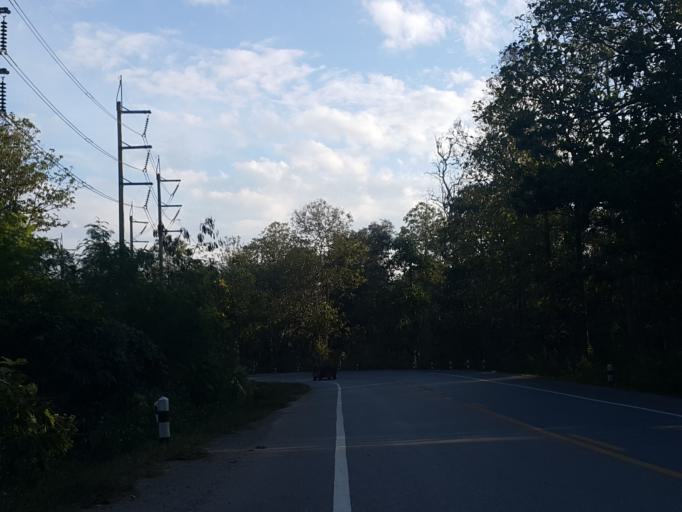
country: TH
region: Lampang
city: Lampang
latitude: 18.4819
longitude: 99.5491
